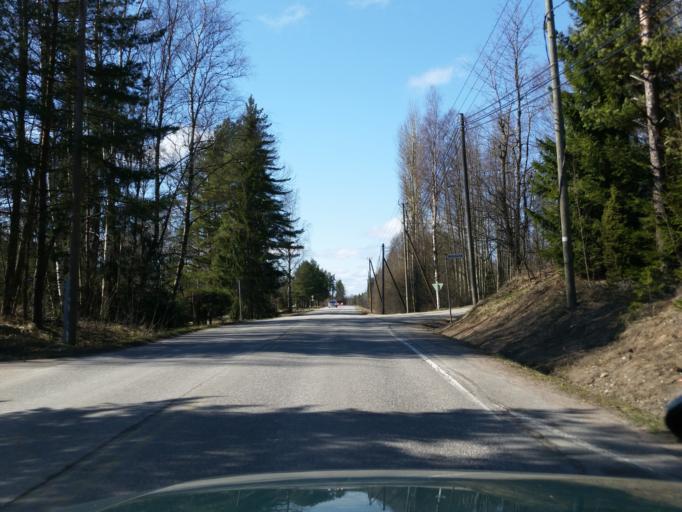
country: FI
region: Uusimaa
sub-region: Helsinki
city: Vihti
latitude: 60.4209
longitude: 24.2734
